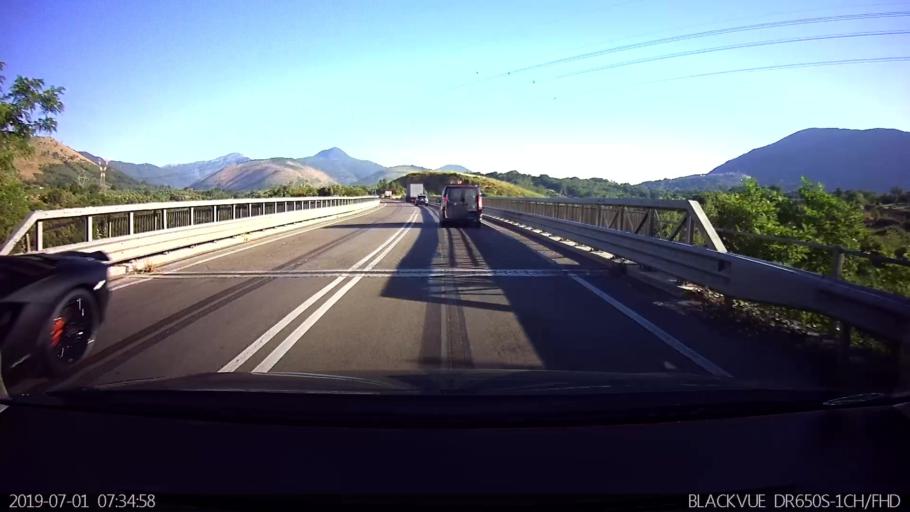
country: IT
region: Latium
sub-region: Provincia di Latina
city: Prossedi
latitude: 41.5210
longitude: 13.2724
